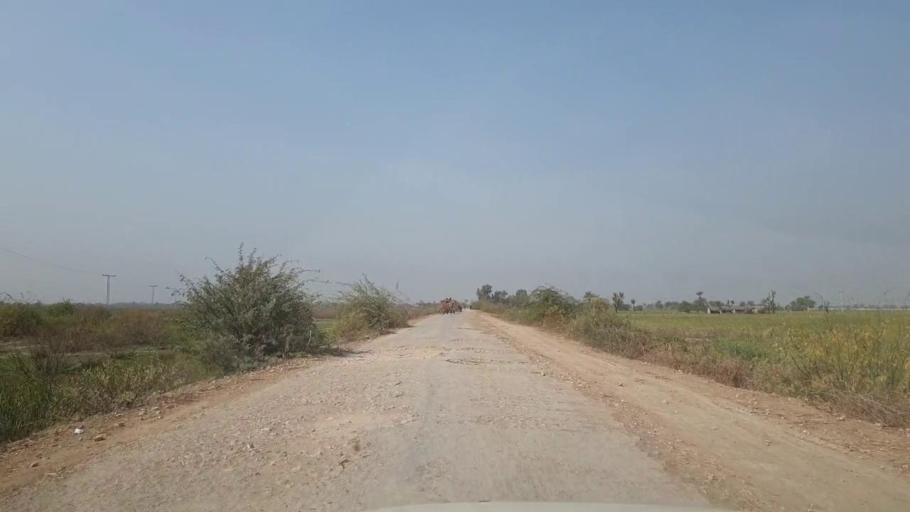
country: PK
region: Sindh
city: Mirpur Khas
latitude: 25.6948
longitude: 69.1478
